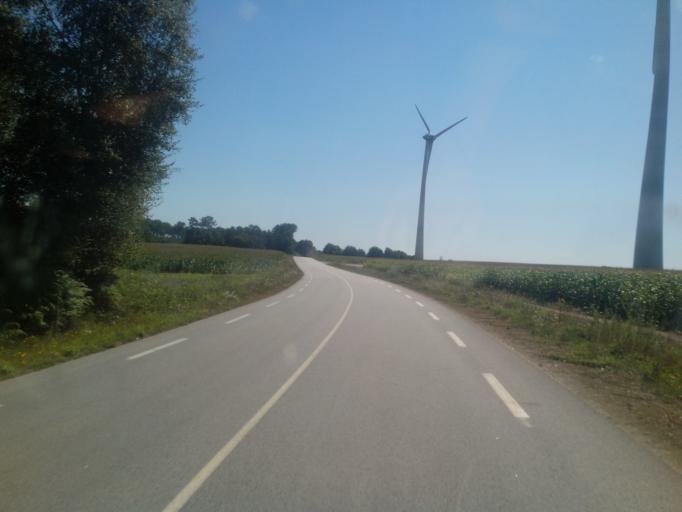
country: FR
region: Brittany
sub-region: Departement du Morbihan
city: Guillac
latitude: 47.8877
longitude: -2.5117
